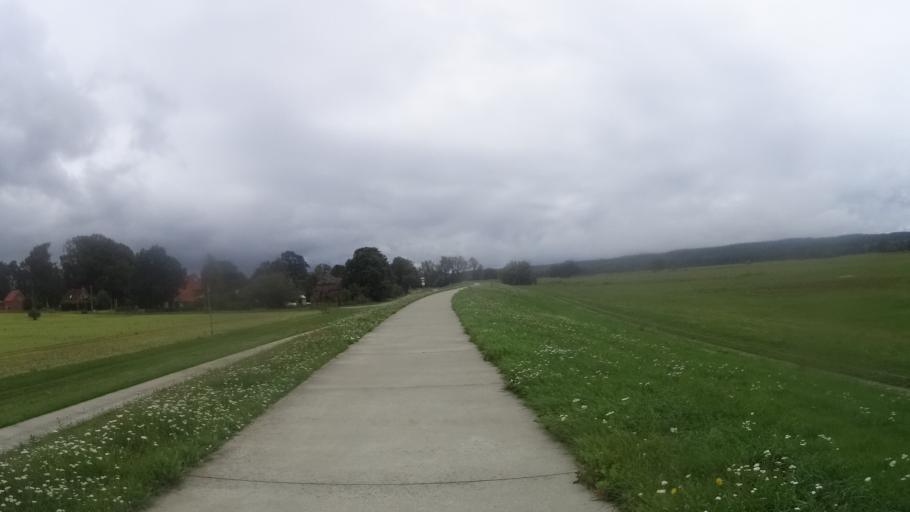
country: DE
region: Lower Saxony
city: Tosterglope
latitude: 53.2754
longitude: 10.8263
